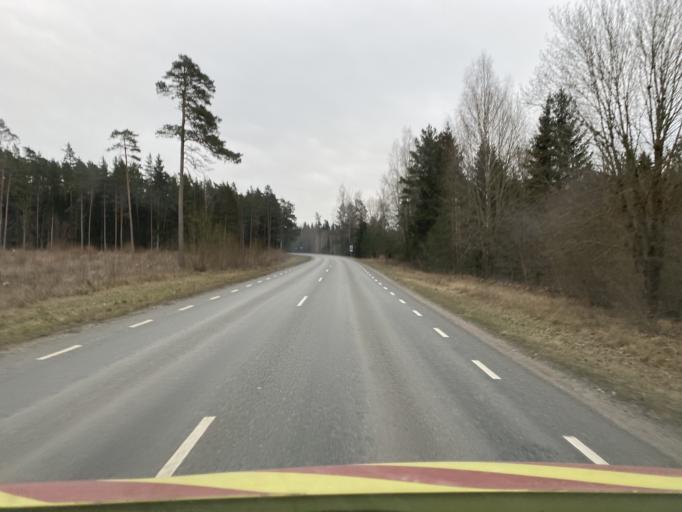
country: EE
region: Laeaene
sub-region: Ridala Parish
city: Uuemoisa
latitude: 59.0048
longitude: 23.6951
